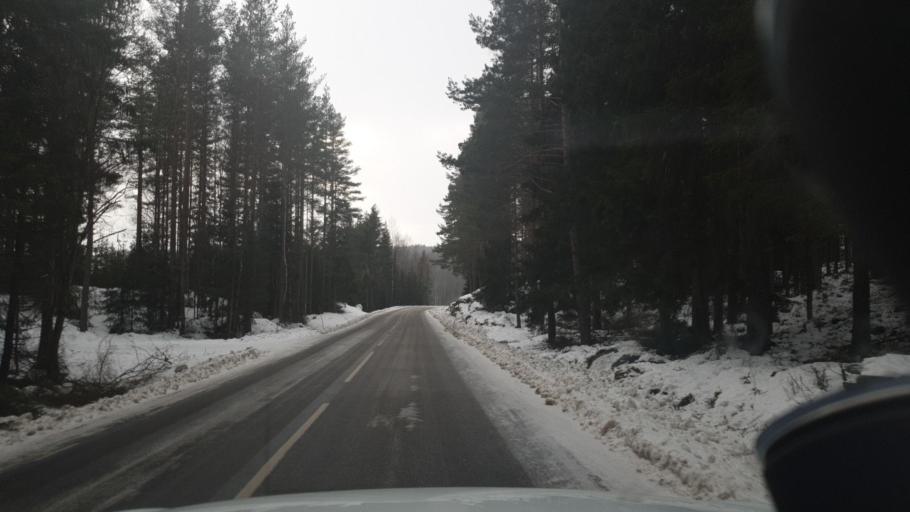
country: SE
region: Vaermland
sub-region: Eda Kommun
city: Amotfors
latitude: 59.5808
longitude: 12.2851
